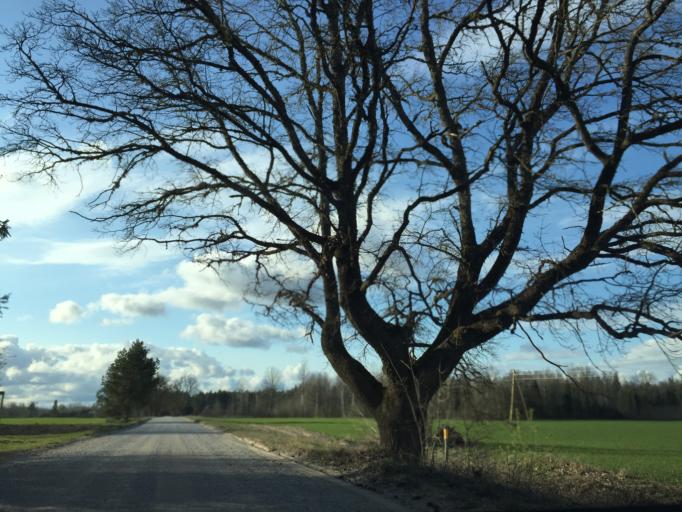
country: LV
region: Burtnieki
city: Matisi
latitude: 57.6189
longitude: 25.0722
